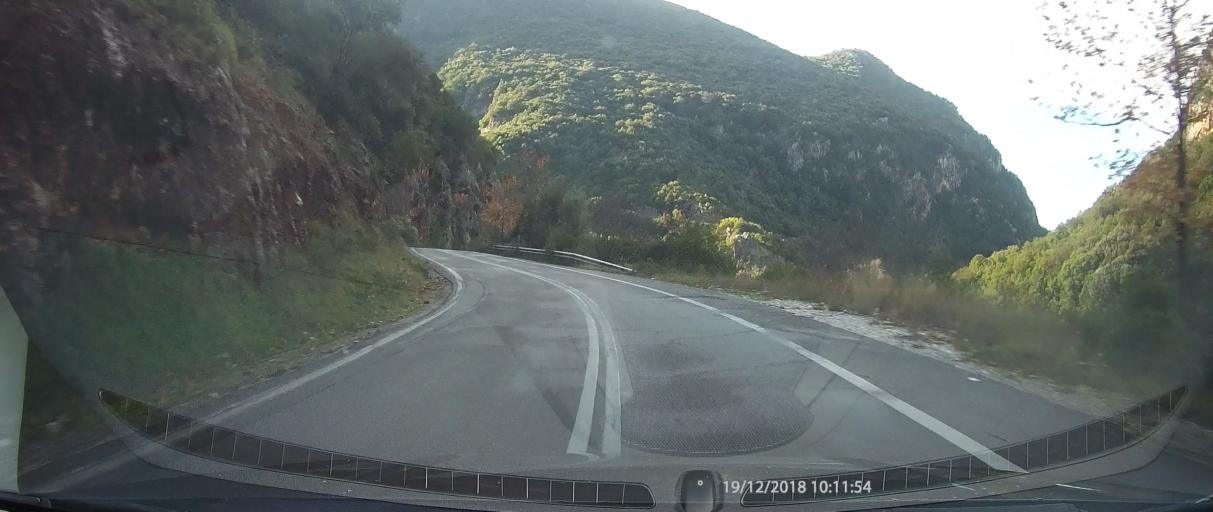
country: GR
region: Peloponnese
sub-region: Nomos Messinias
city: Kalamata
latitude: 37.0938
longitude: 22.1745
